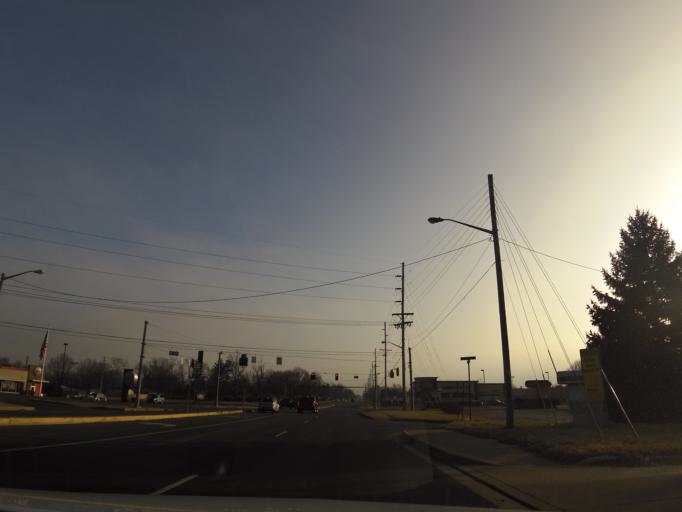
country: US
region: Indiana
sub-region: Bartholomew County
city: Columbus
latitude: 39.2231
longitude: -85.8920
